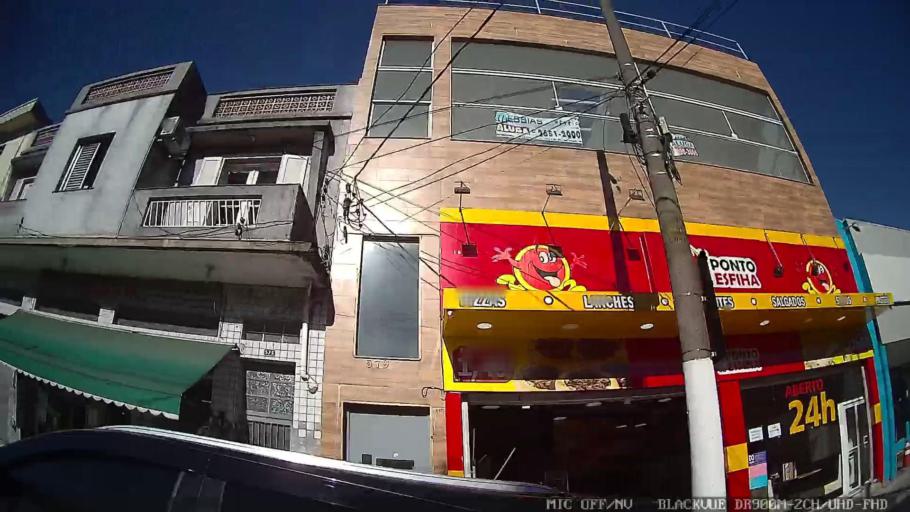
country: BR
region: Sao Paulo
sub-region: Guarulhos
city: Guarulhos
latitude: -23.5375
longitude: -46.5257
